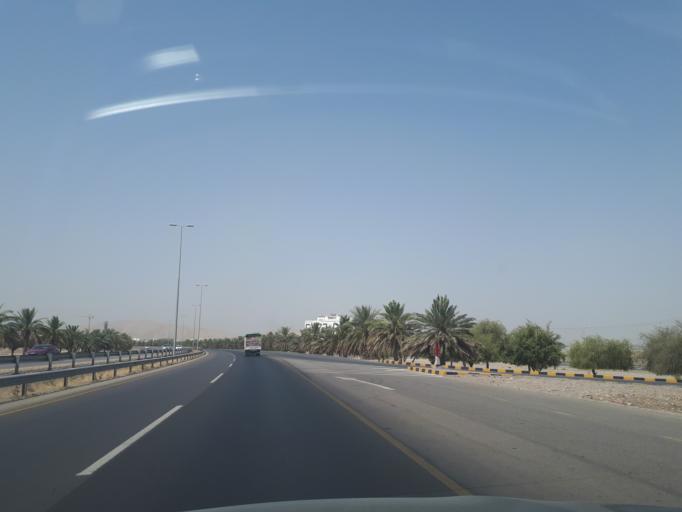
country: OM
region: Muhafazat Masqat
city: As Sib al Jadidah
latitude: 23.5898
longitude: 58.2015
